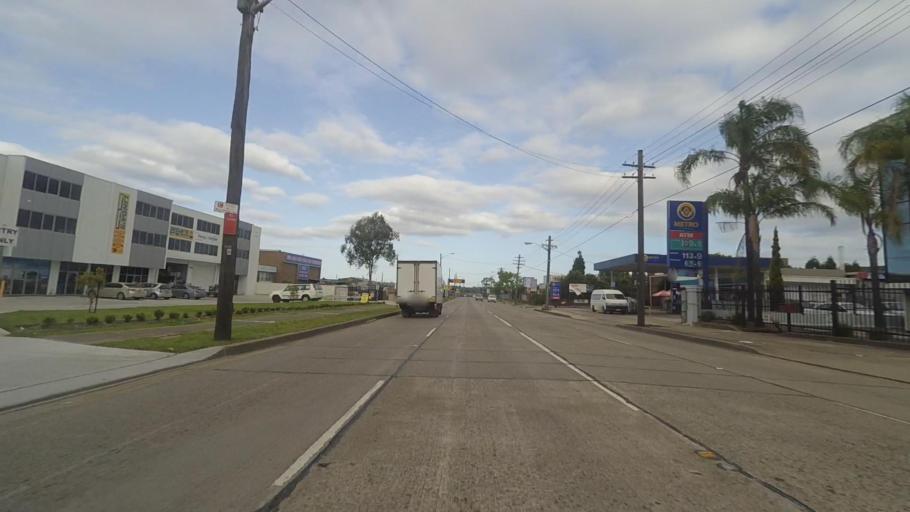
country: AU
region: New South Wales
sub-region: Bankstown
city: Bankstown
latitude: -33.9341
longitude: 151.0309
